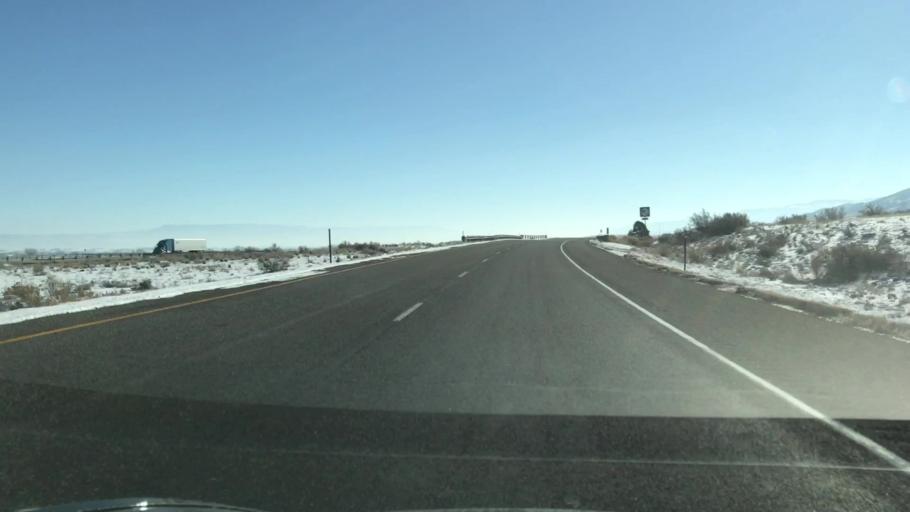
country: US
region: Colorado
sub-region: Mesa County
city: Loma
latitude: 39.2146
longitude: -108.8699
